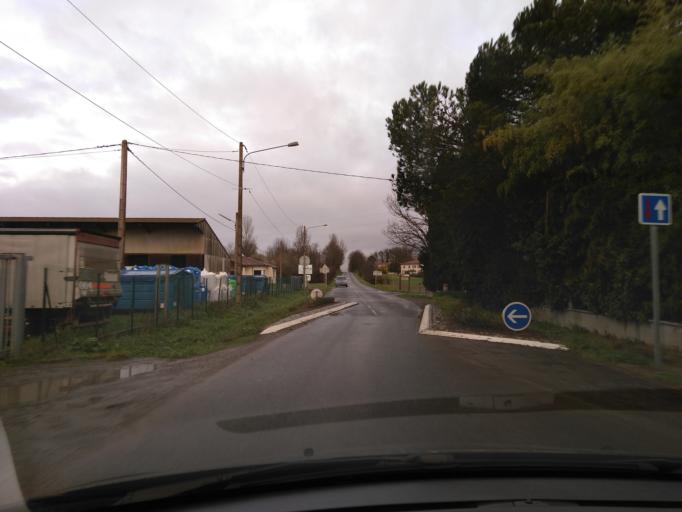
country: FR
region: Midi-Pyrenees
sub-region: Departement de la Haute-Garonne
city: Montesquieu-Volvestre
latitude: 43.1472
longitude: 1.3017
